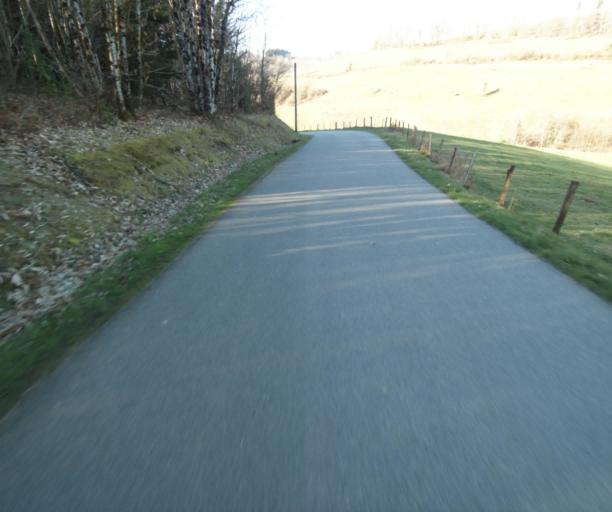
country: FR
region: Limousin
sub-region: Departement de la Correze
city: Seilhac
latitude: 45.3818
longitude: 1.7505
